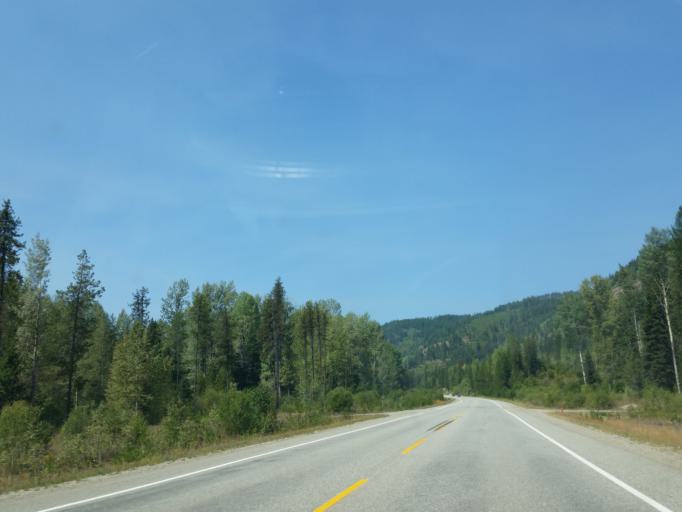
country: CA
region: British Columbia
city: Castlegar
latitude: 49.2975
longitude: -117.8353
